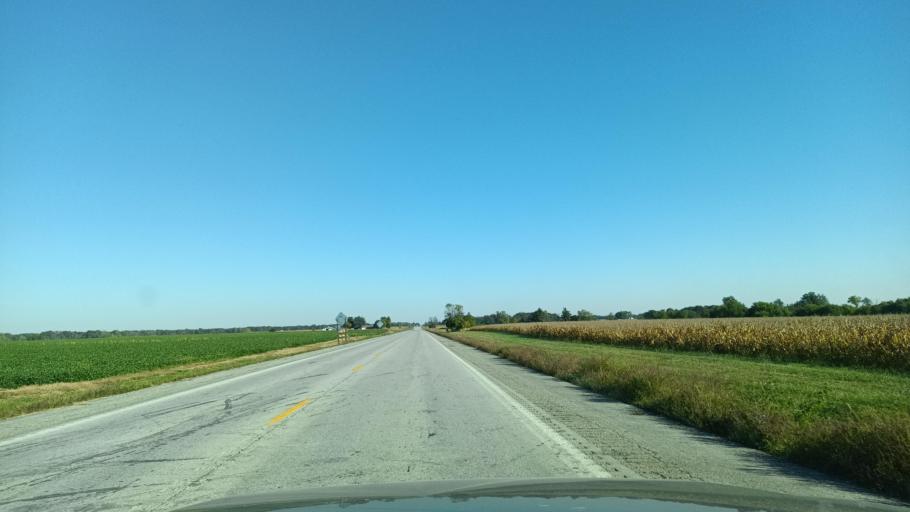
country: US
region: Missouri
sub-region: Audrain County
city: Vandalia
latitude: 39.2845
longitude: -91.6441
